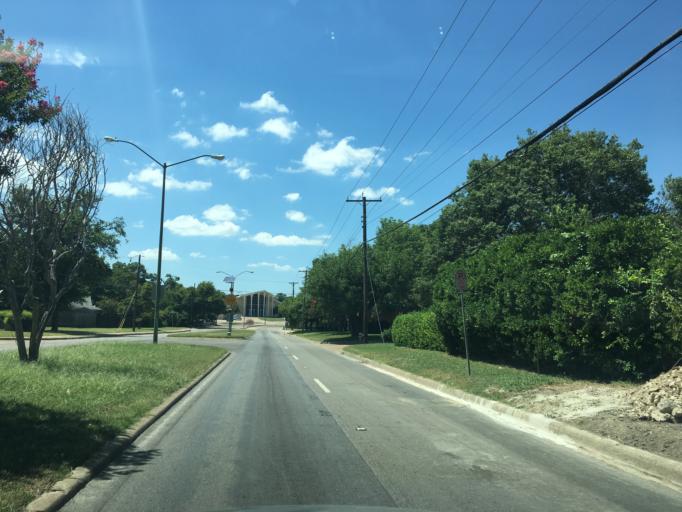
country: US
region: Texas
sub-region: Dallas County
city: Garland
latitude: 32.8513
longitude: -96.6997
